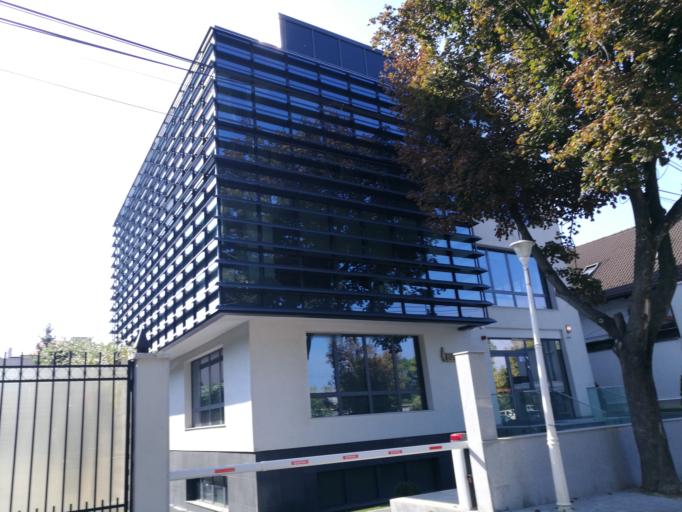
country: RO
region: Bucuresti
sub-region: Municipiul Bucuresti
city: Bucuresti
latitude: 44.4826
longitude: 26.0682
